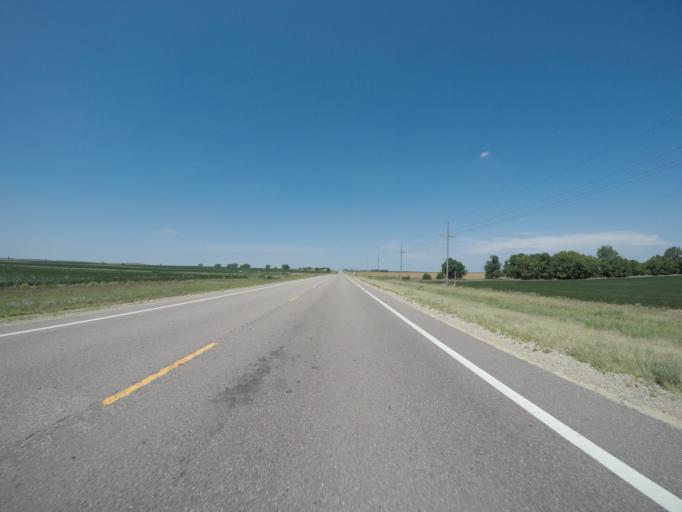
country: US
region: Kansas
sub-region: Osborne County
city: Osborne
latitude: 39.5099
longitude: -98.6357
